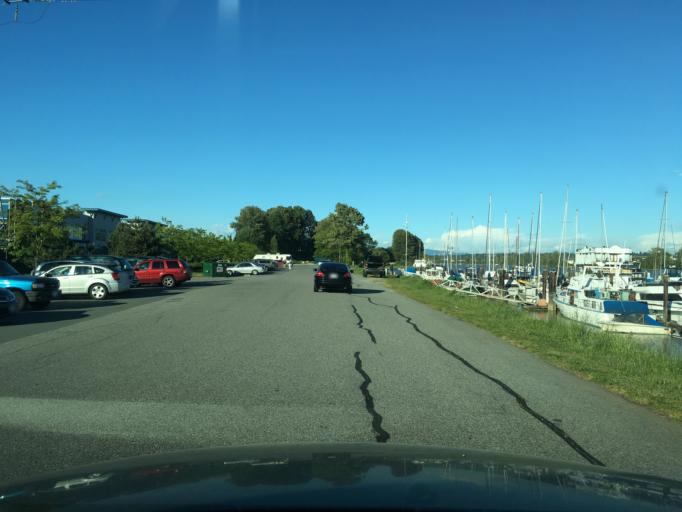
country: CA
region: British Columbia
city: Delta
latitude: 49.1638
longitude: -122.9880
